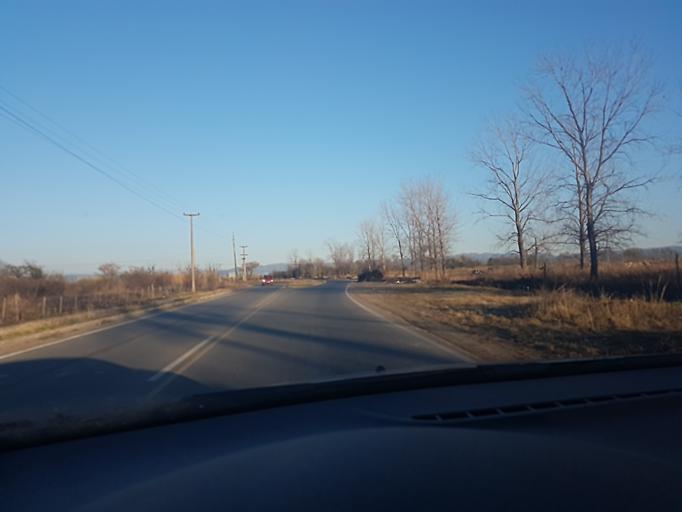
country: AR
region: Cordoba
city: Villa Allende
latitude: -31.3158
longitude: -64.2228
